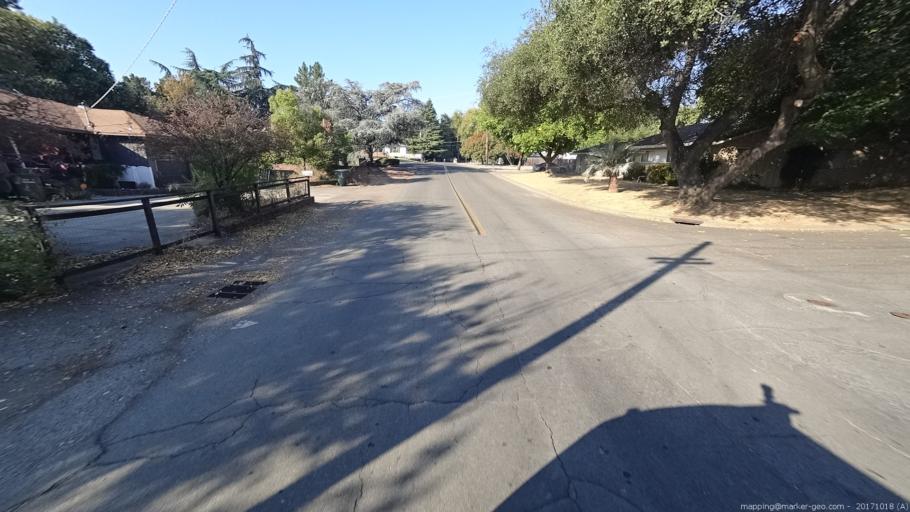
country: US
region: California
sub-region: Shasta County
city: Redding
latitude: 40.5613
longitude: -122.3718
